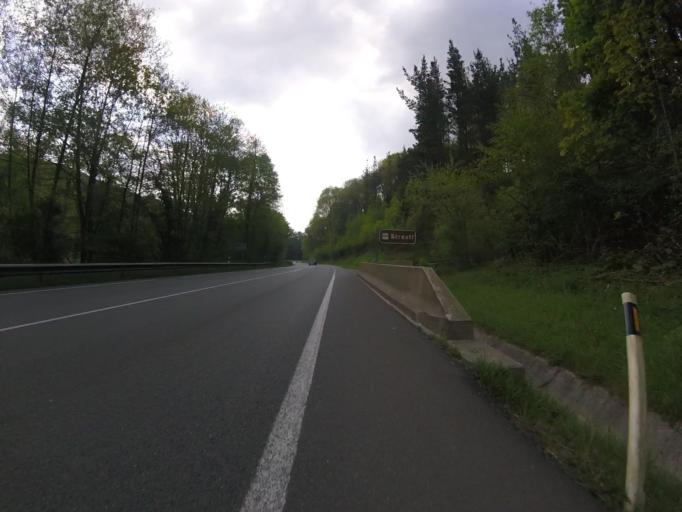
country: ES
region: Basque Country
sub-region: Provincia de Guipuzcoa
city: Azkoitia
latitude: 43.1866
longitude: -2.3268
